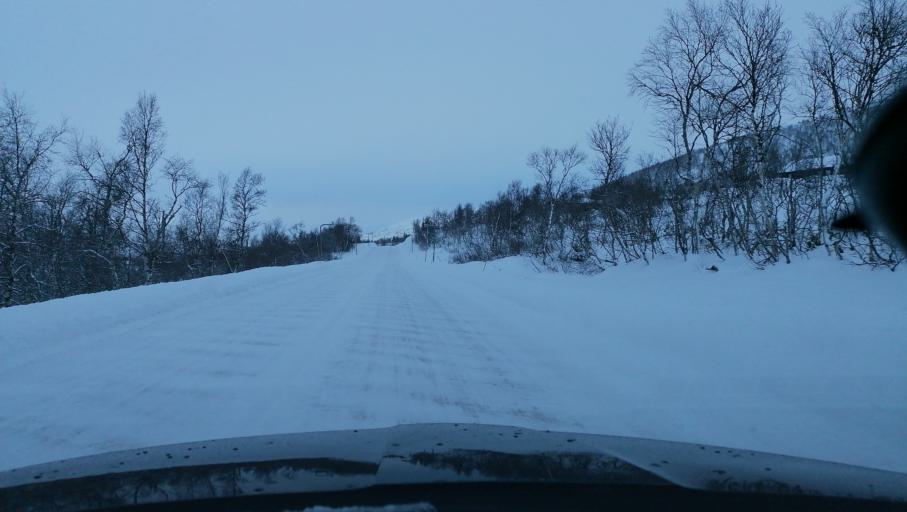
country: NO
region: Aust-Agder
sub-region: Bykle
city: Hovden
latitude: 59.6344
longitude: 7.4537
